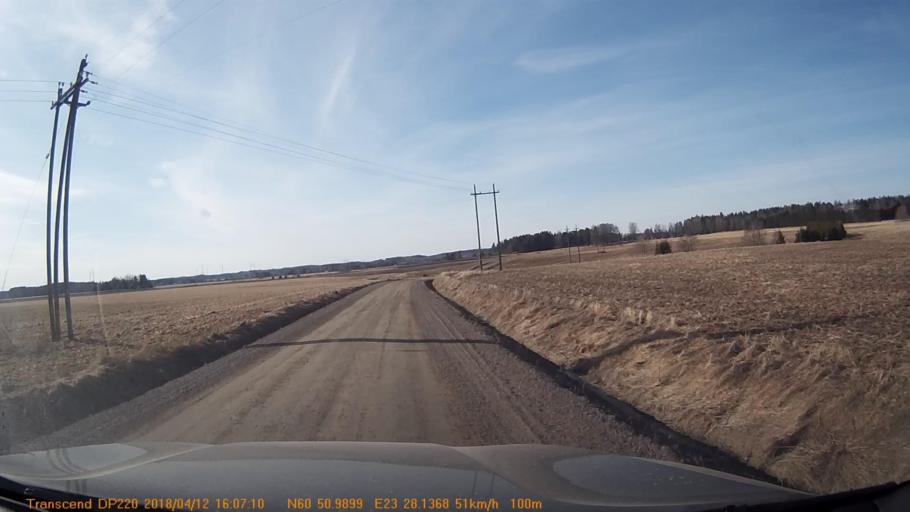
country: FI
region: Haeme
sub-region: Forssa
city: Jokioinen
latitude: 60.8499
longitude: 23.4686
